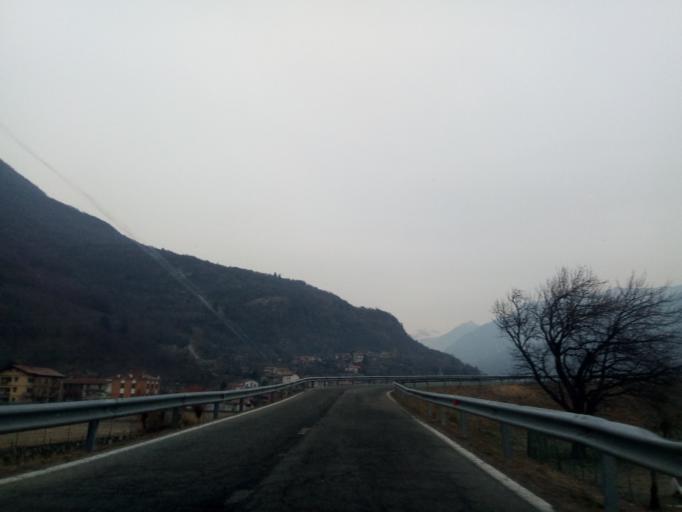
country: IT
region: Piedmont
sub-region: Provincia di Torino
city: Quassolo
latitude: 45.5193
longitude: 7.8343
